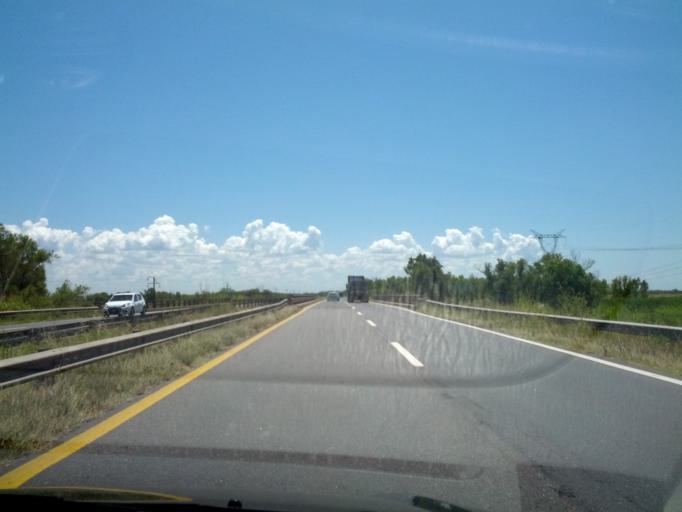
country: AR
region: Entre Rios
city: Villa Paranacito
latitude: -33.7579
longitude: -58.8621
